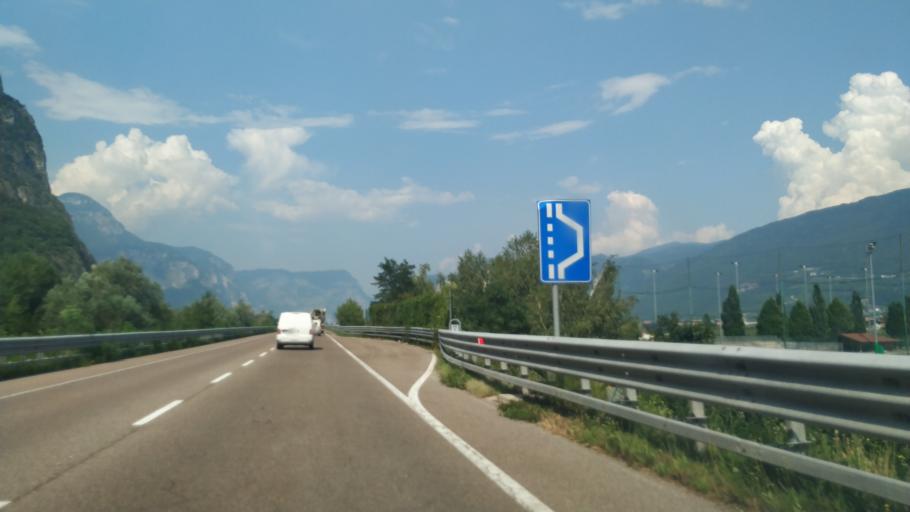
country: IT
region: Trentino-Alto Adige
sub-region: Provincia di Trento
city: Fai della Paganella
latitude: 46.1681
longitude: 11.0852
